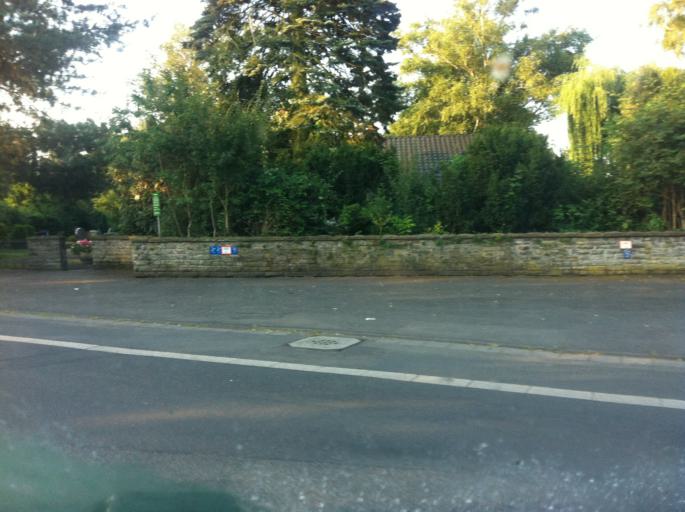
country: DE
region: Rheinland-Pfalz
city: Erpel
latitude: 50.5759
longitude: 7.2443
